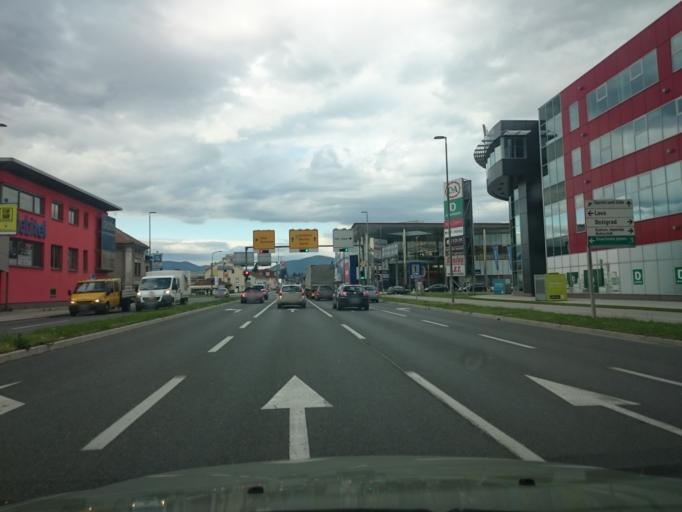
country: SI
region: Celje
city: Celje
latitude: 46.2401
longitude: 15.2749
